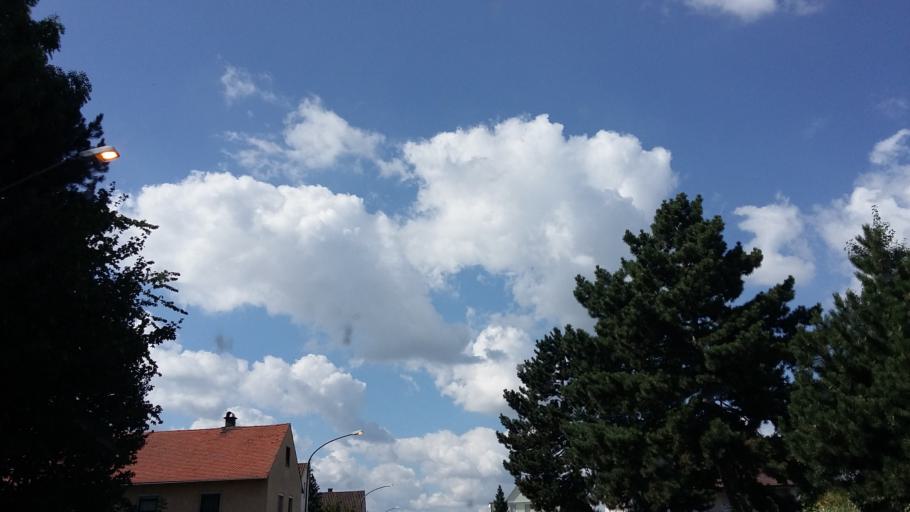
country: DE
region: Bavaria
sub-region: Swabia
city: Neu-Ulm
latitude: 48.3827
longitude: 10.0246
